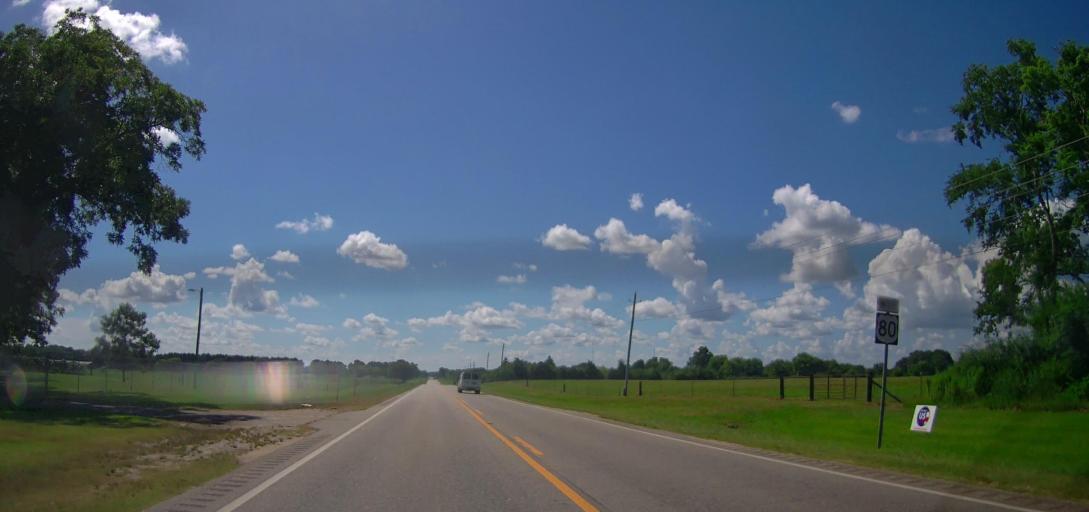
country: US
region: Alabama
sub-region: Elmore County
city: Tallassee
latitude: 32.3863
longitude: -85.8848
